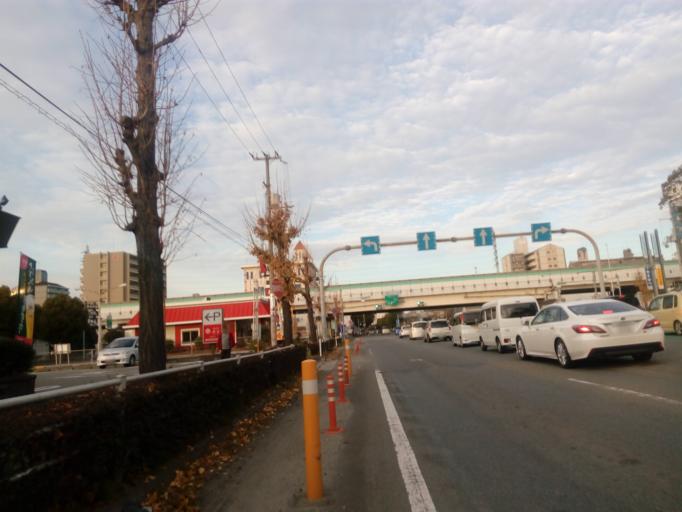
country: JP
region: Hyogo
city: Himeji
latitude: 34.8109
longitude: 134.6818
